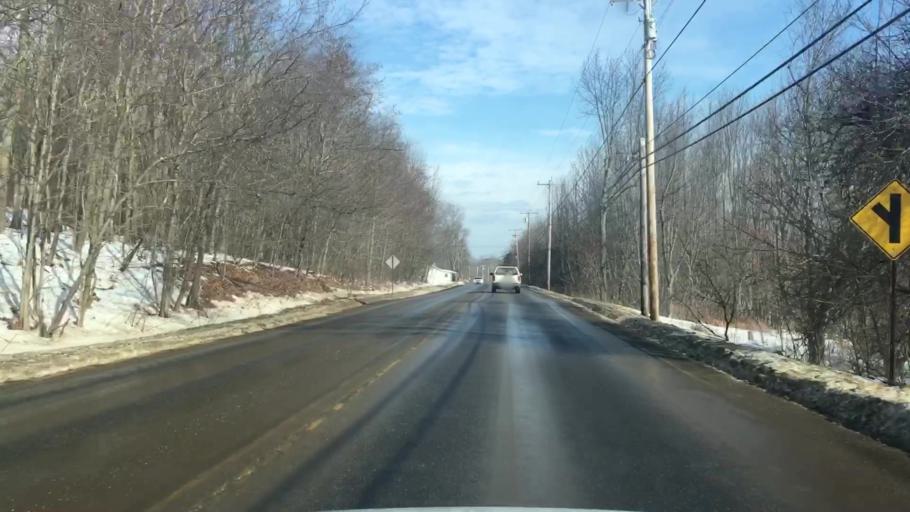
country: US
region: Maine
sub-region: Penobscot County
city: Hermon
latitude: 44.8339
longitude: -68.8783
